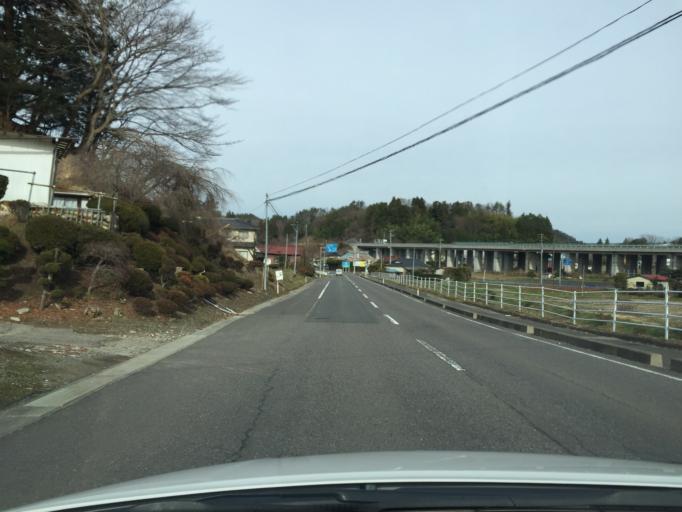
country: JP
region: Fukushima
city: Funehikimachi-funehiki
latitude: 37.3610
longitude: 140.6066
